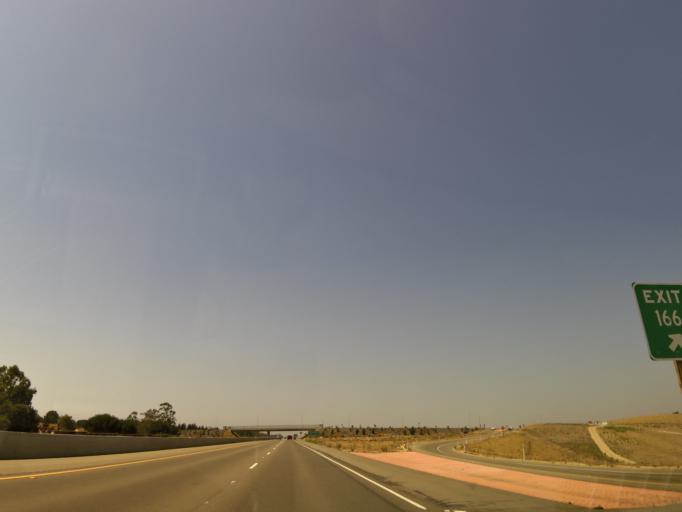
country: US
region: California
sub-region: Santa Barbara County
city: Orcutt
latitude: 34.8769
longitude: -120.4059
